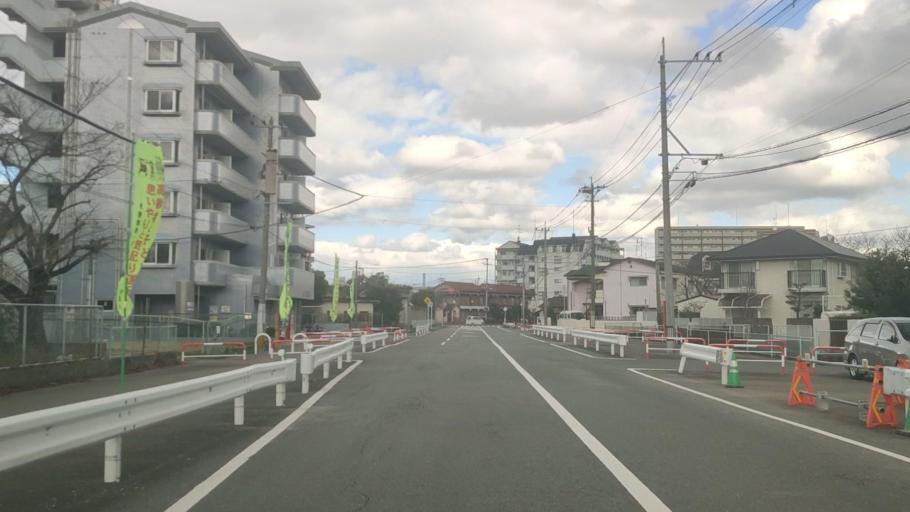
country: JP
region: Fukuoka
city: Fukuoka-shi
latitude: 33.6151
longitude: 130.4311
